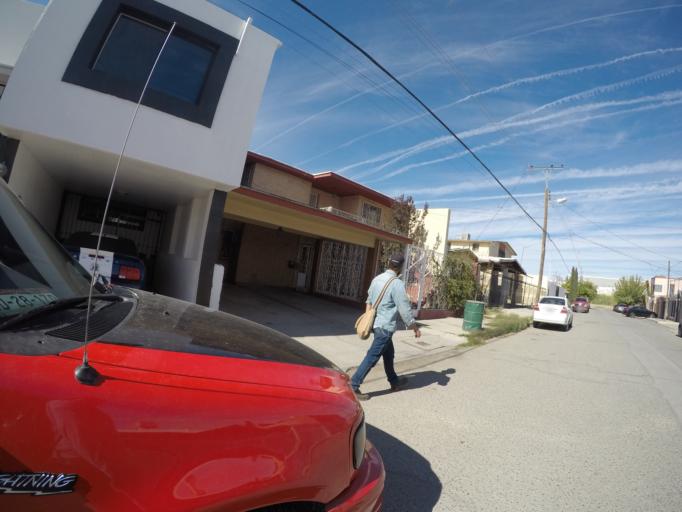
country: MX
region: Chihuahua
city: Ciudad Juarez
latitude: 31.7337
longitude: -106.4435
